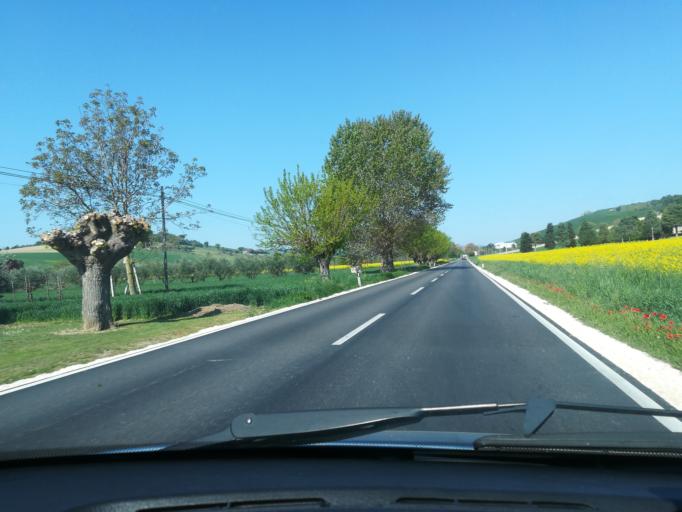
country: IT
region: The Marches
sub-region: Provincia di Macerata
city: Villa Potenza
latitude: 43.3268
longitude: 13.4010
